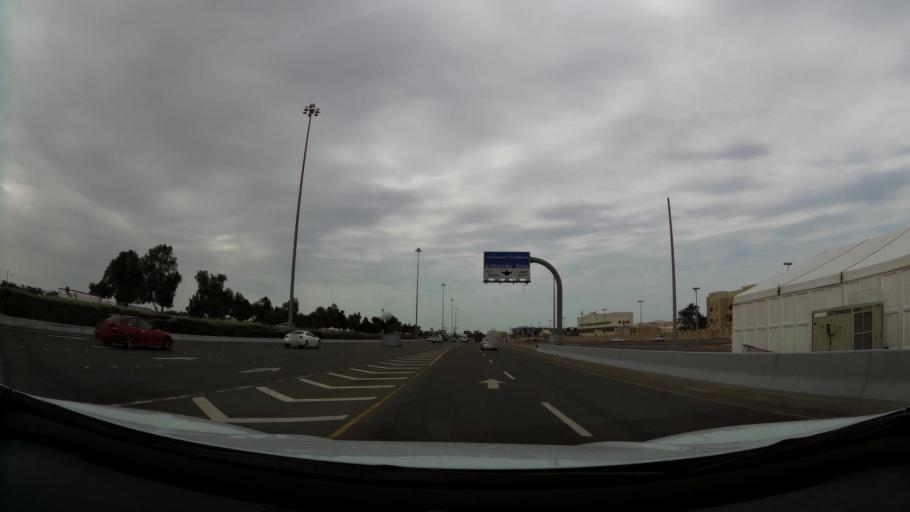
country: AE
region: Abu Dhabi
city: Abu Dhabi
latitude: 24.4182
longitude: 54.4328
